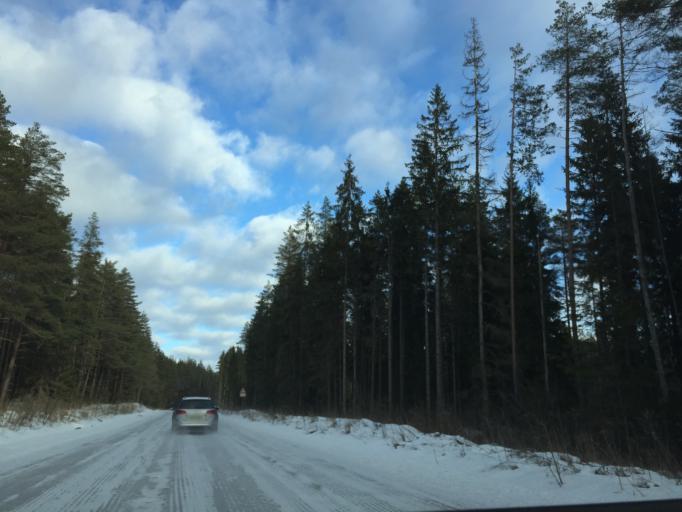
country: LV
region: Ogre
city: Jumprava
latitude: 56.5721
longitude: 24.9365
